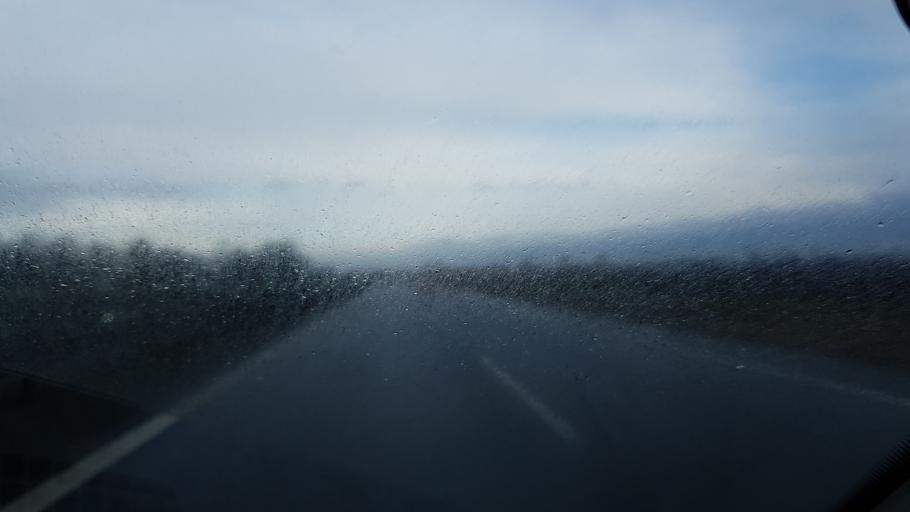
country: CZ
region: Olomoucky
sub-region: Okres Prostejov
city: Prostejov
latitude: 49.4541
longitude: 17.1166
